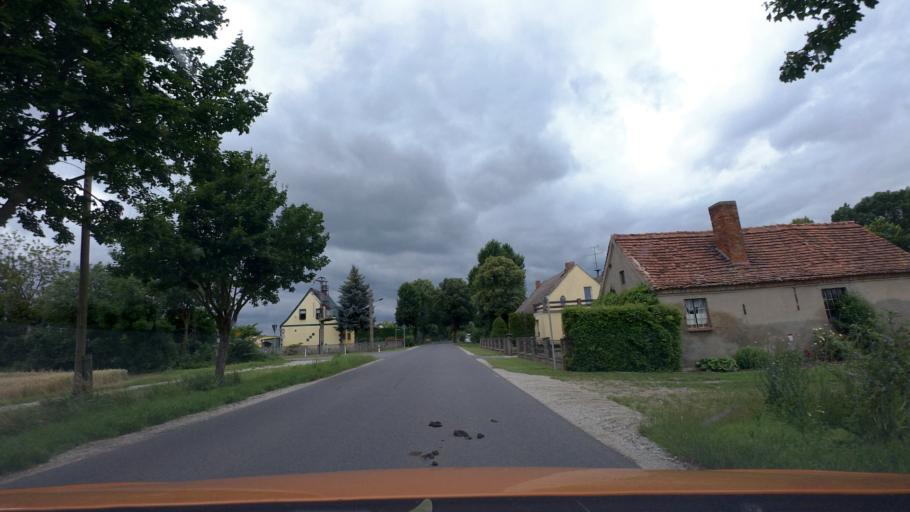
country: DE
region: Brandenburg
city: Neulewin
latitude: 52.7376
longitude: 14.2654
